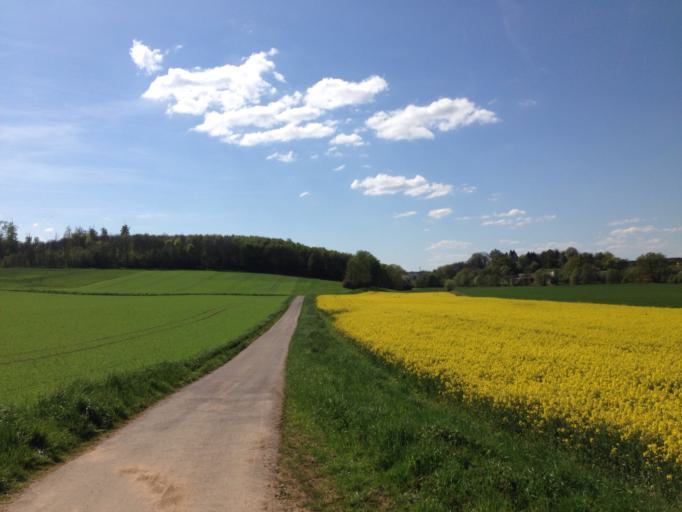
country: DE
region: Hesse
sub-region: Regierungsbezirk Giessen
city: Laubach
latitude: 50.5470
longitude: 8.9445
